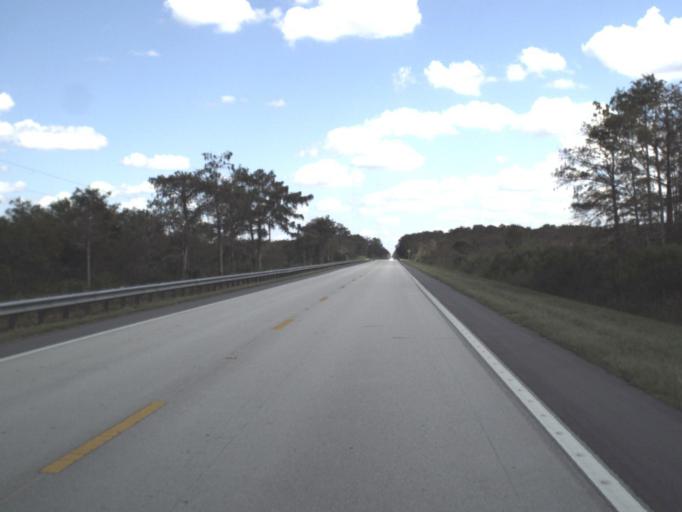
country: US
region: Florida
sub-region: Miami-Dade County
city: Kendall West
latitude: 25.8588
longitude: -81.0525
